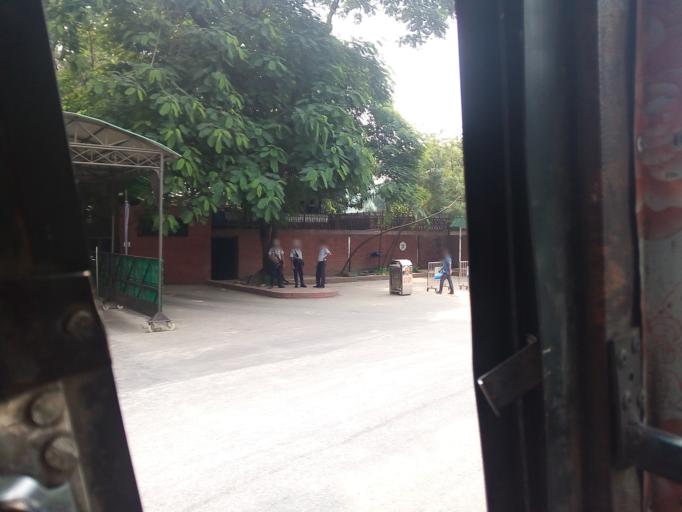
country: BD
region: Dhaka
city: Azimpur
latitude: 23.7656
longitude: 90.3704
